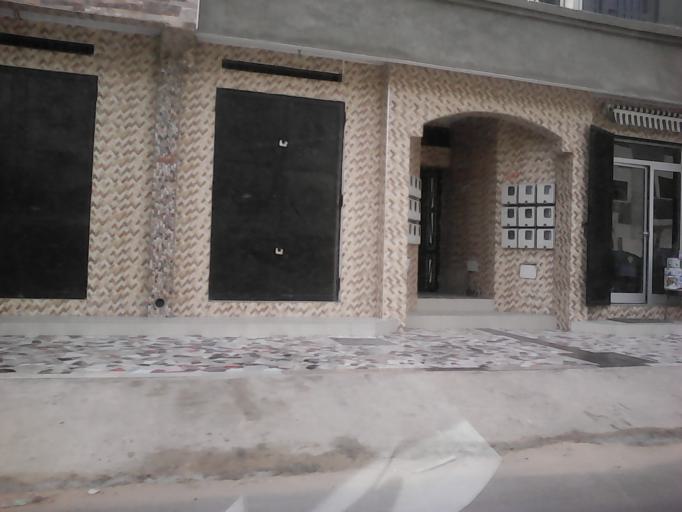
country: SN
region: Dakar
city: Grand Dakar
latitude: 14.7334
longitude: -17.4290
